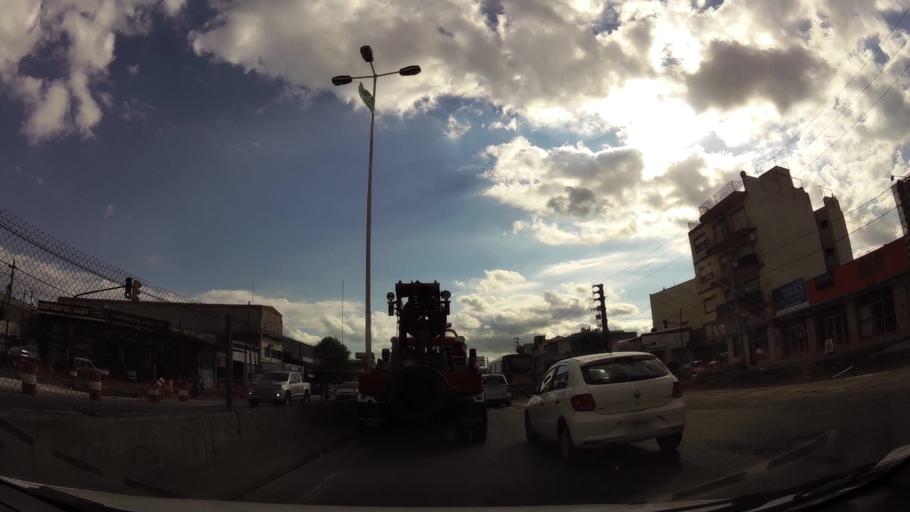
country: AR
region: Buenos Aires
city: San Justo
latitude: -34.6905
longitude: -58.5692
